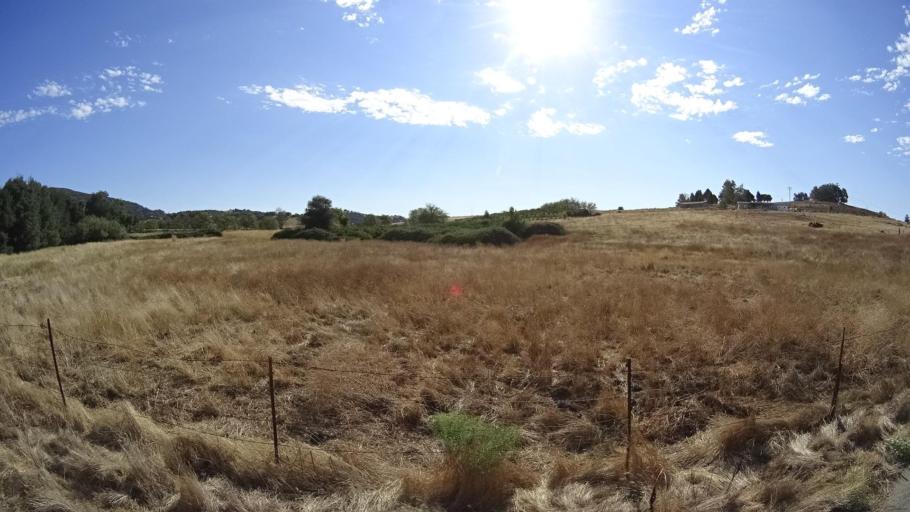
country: US
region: California
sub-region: San Diego County
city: San Diego Country Estates
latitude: 33.1689
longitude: -116.7604
